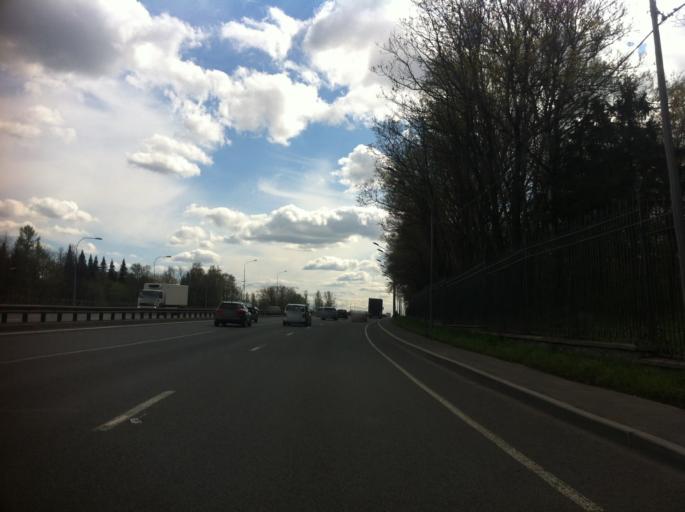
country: RU
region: St.-Petersburg
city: Aleksandrovskaya
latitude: 59.7706
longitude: 30.3323
